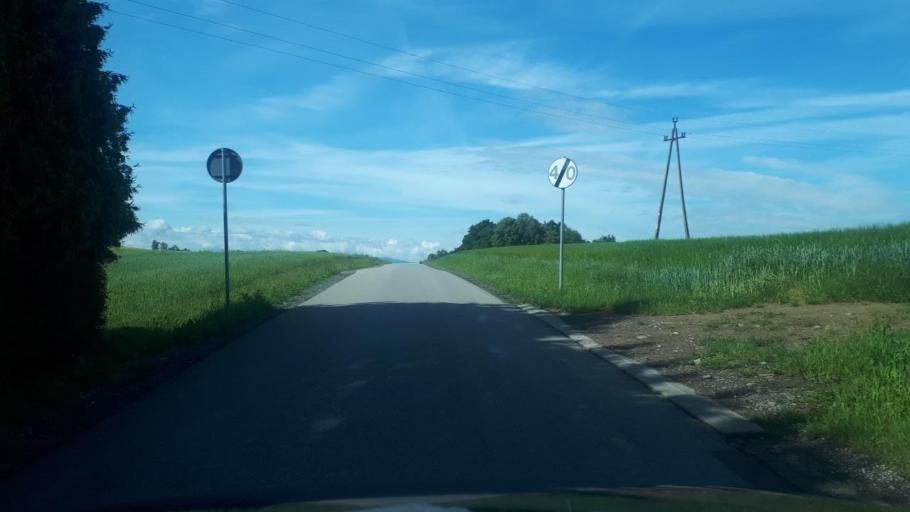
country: PL
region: Silesian Voivodeship
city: Janowice
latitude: 49.9039
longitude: 19.1133
